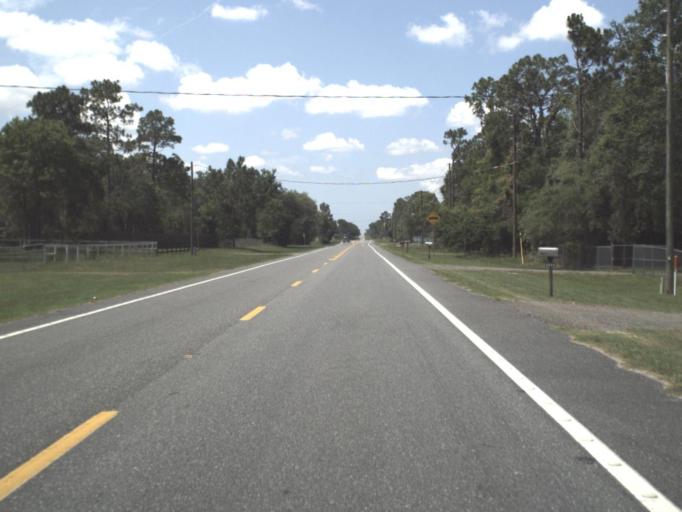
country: US
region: Florida
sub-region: Levy County
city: Williston Highlands
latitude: 29.2944
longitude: -82.5333
